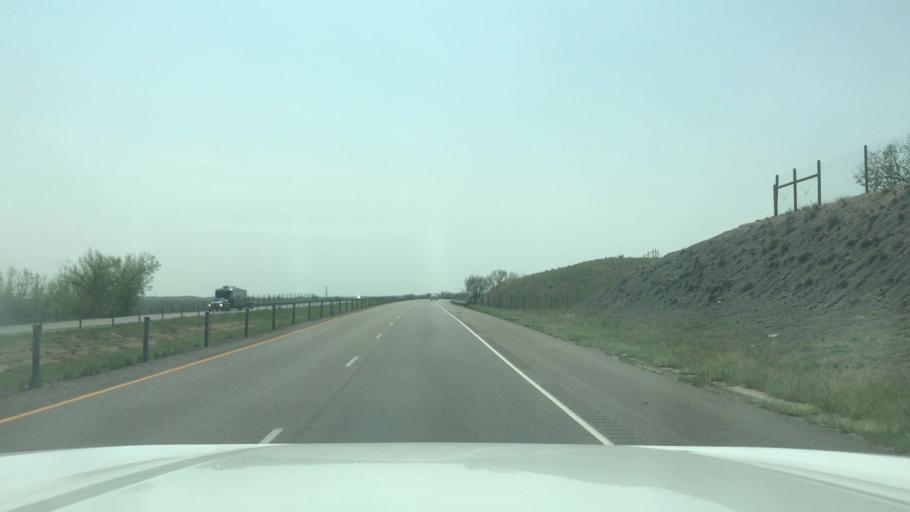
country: US
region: Colorado
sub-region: El Paso County
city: Fountain
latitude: 38.6465
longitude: -104.6951
